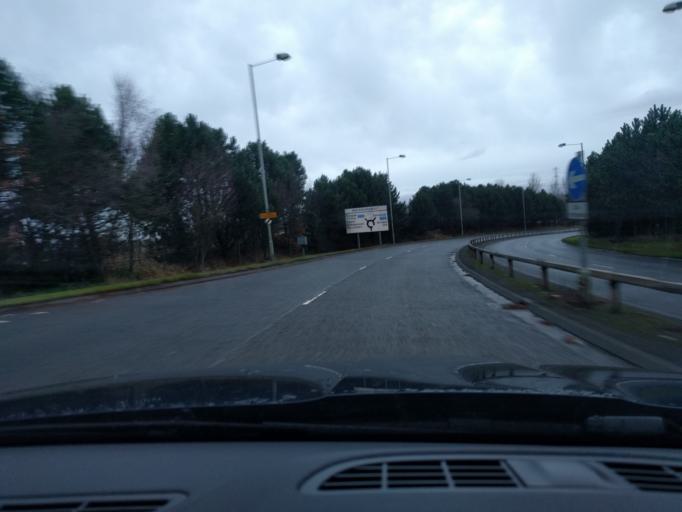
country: GB
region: Scotland
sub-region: Falkirk
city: Falkirk
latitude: 55.9979
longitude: -3.7539
